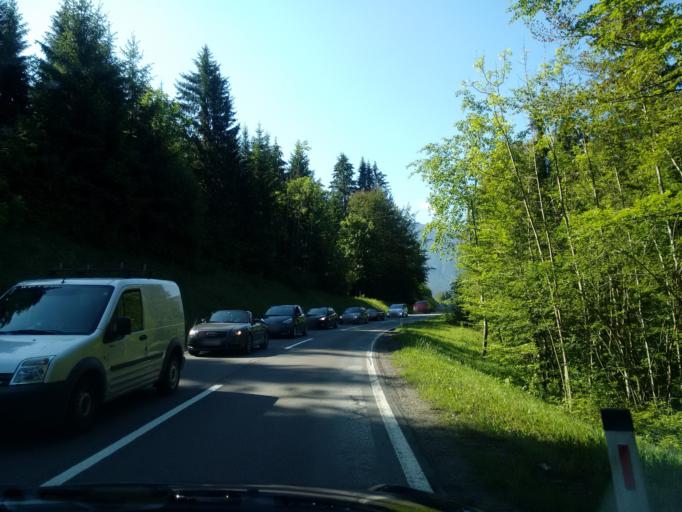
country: AT
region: Styria
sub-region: Politischer Bezirk Liezen
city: Altaussee
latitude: 47.6256
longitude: 13.7611
